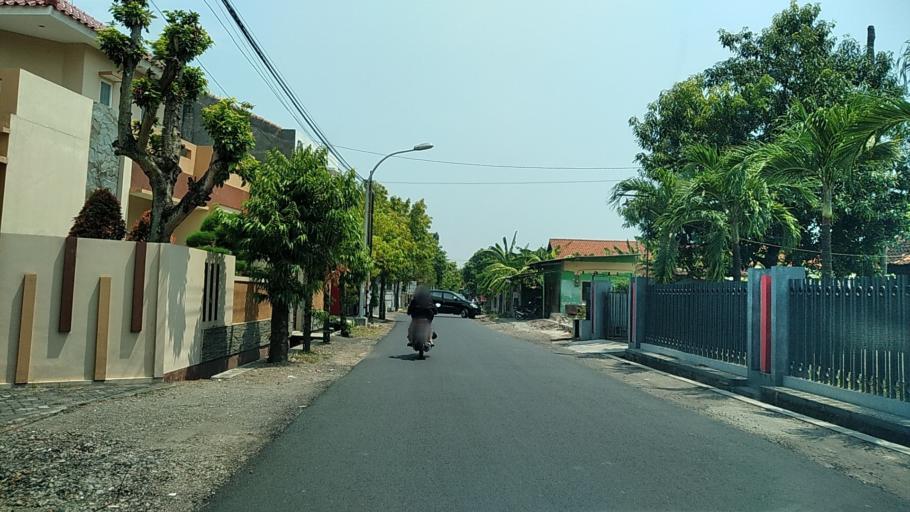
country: ID
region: Central Java
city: Mranggen
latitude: -7.0076
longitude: 110.4764
